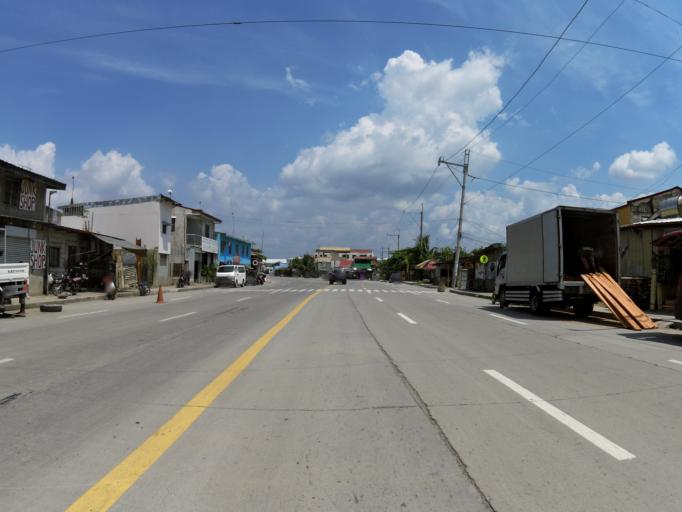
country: PH
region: Calabarzon
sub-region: Province of Rizal
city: Taytay
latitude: 14.5333
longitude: 121.1114
